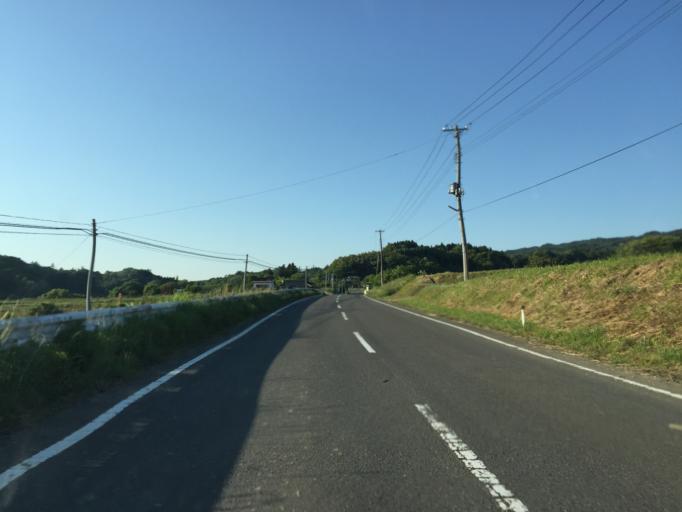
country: JP
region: Fukushima
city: Ishikawa
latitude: 36.9816
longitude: 140.4344
